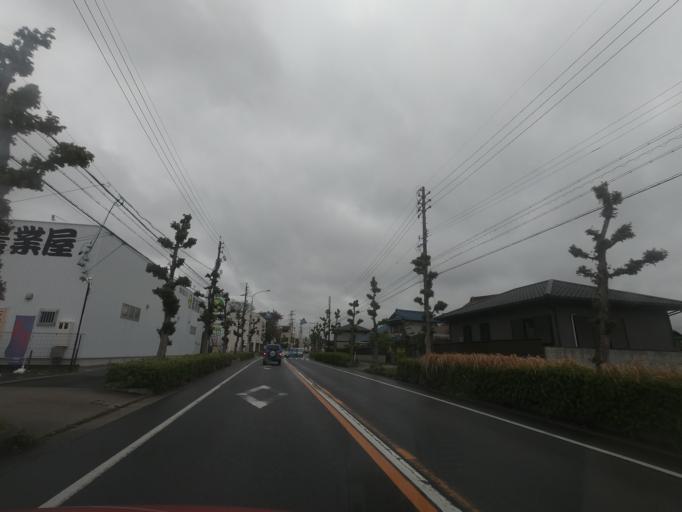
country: JP
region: Aichi
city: Kasugai
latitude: 35.2686
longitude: 136.9871
